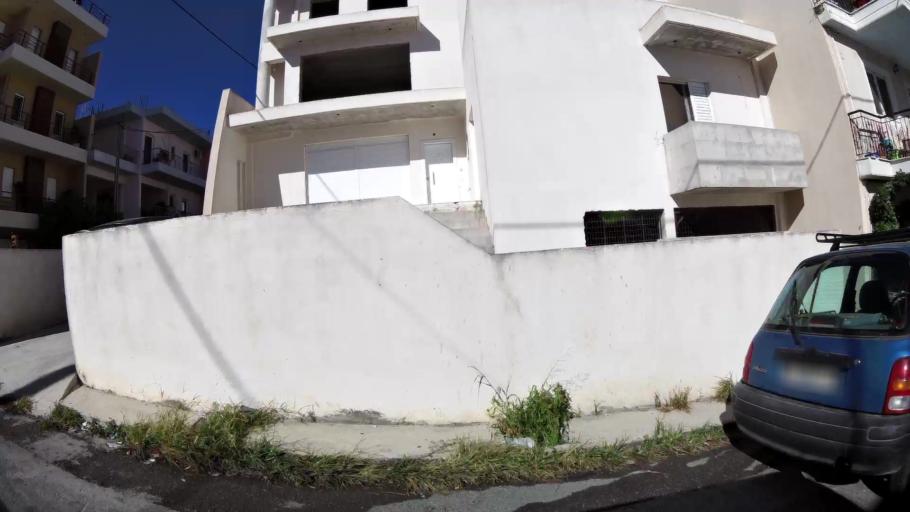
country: GR
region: Attica
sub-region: Nomarchia Anatolikis Attikis
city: Koropi
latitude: 37.8948
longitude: 23.8770
